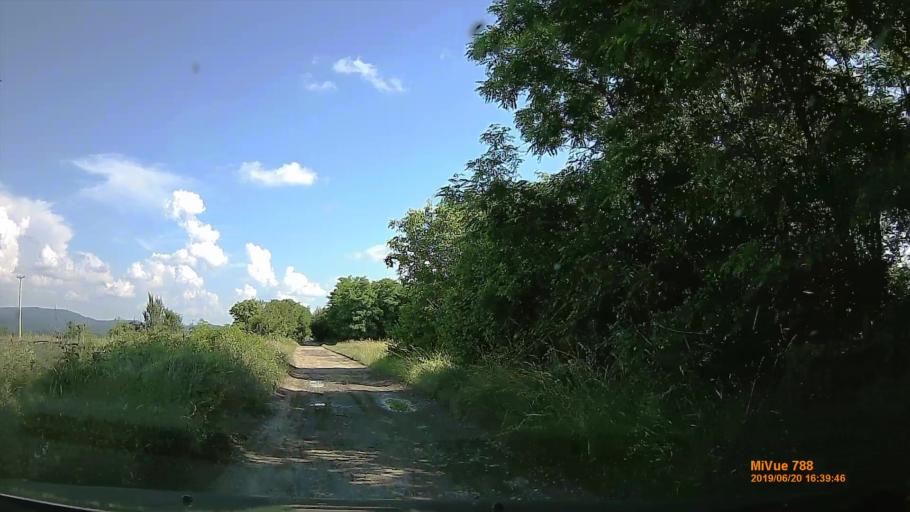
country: HU
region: Baranya
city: Buekkoesd
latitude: 46.1692
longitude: 18.0333
